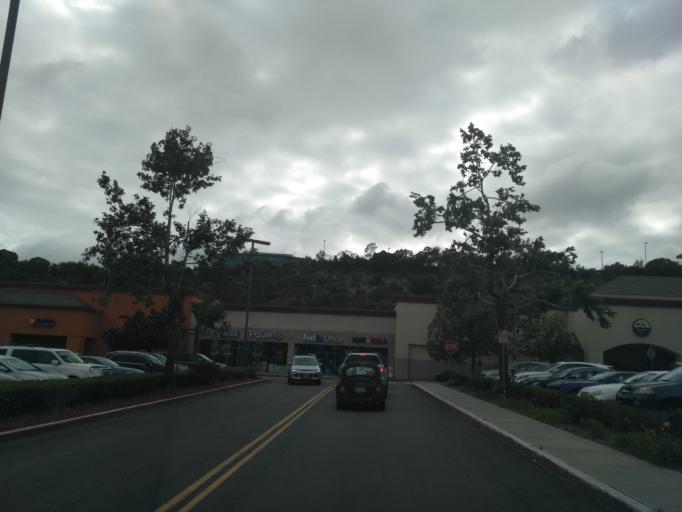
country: US
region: California
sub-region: San Diego County
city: La Mesa
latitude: 32.8070
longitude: -117.1155
